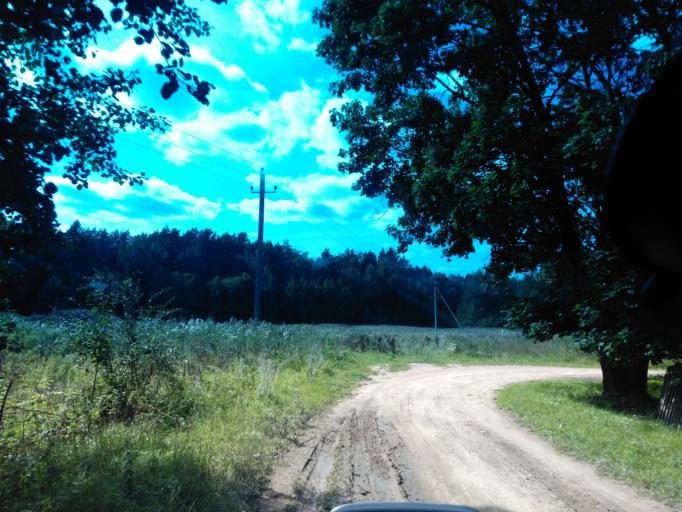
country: BY
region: Minsk
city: Stan'kava
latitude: 53.6241
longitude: 27.3146
